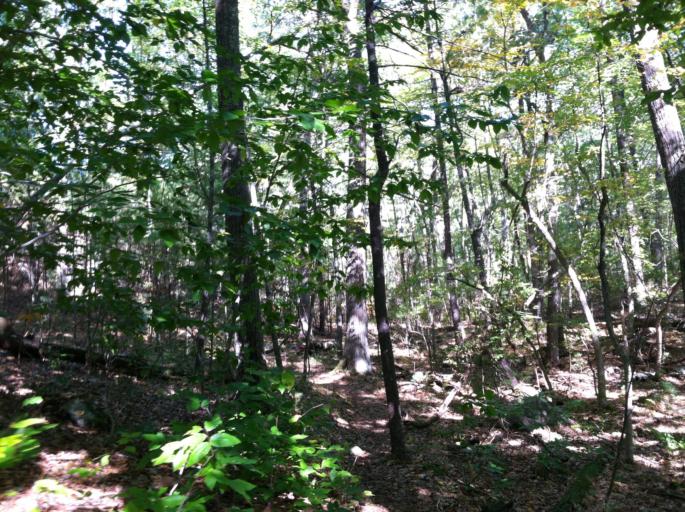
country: US
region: Massachusetts
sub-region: Middlesex County
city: Carlisle
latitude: 42.5328
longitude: -71.3550
